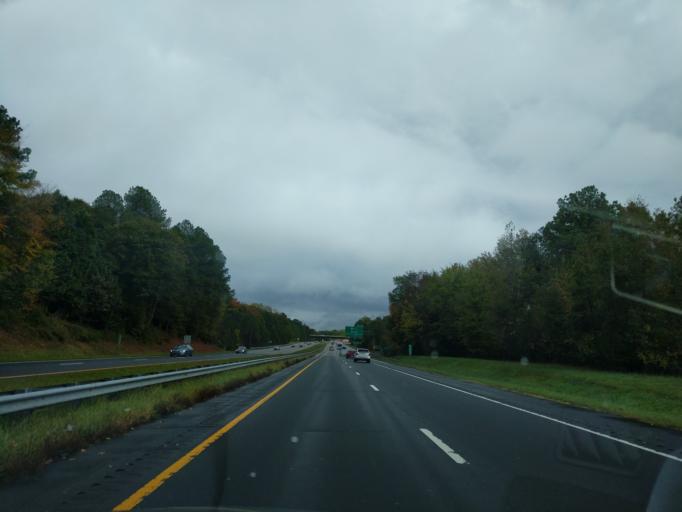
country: US
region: North Carolina
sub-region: Durham County
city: Durham
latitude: 36.0380
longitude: -78.9882
